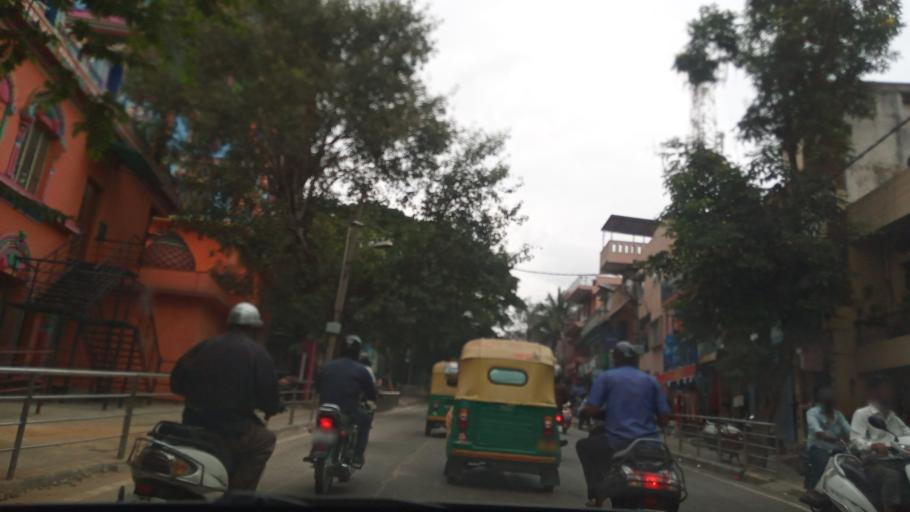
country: IN
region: Karnataka
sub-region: Bangalore Urban
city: Bangalore
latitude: 13.0084
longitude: 77.5448
